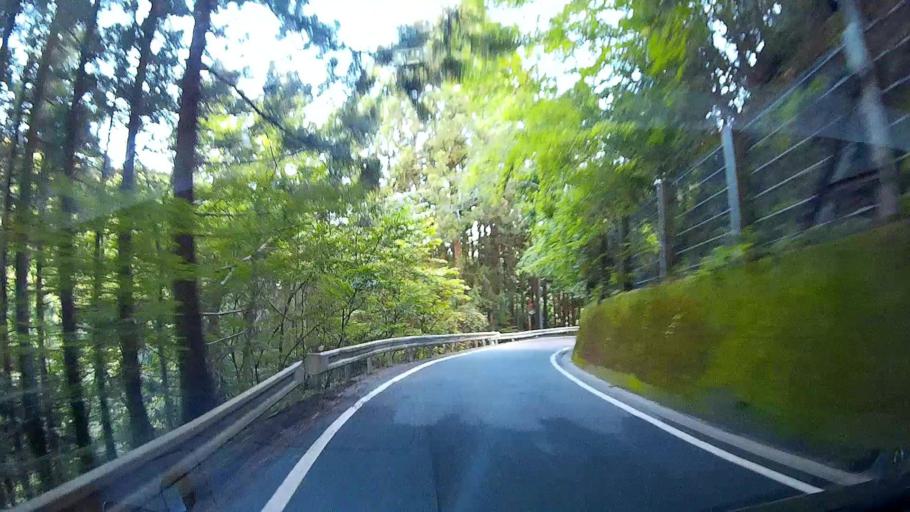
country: JP
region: Shizuoka
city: Shizuoka-shi
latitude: 35.1592
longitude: 138.2567
